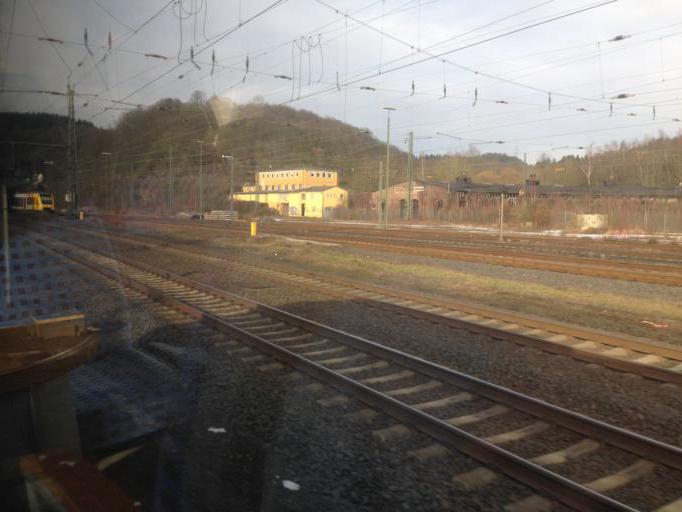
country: DE
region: Hesse
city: Dillenburg
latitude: 50.7324
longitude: 8.2952
